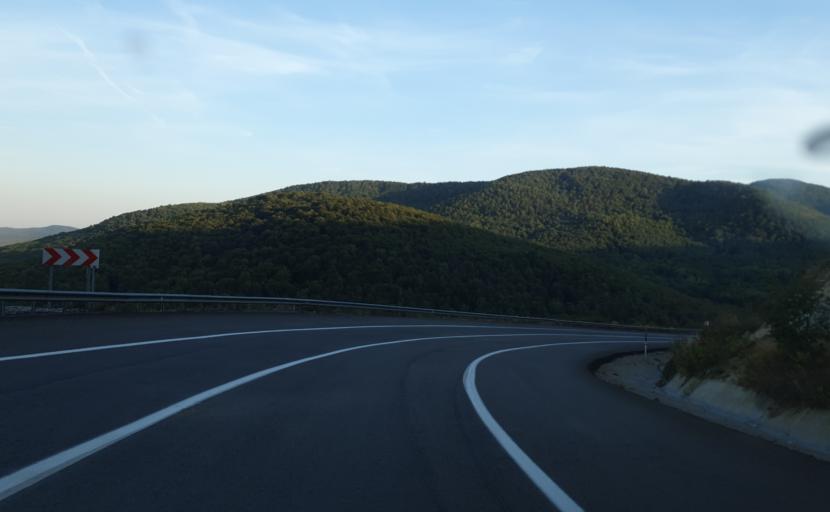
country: TR
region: Kirklareli
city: Sergen
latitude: 41.8133
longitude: 27.7472
